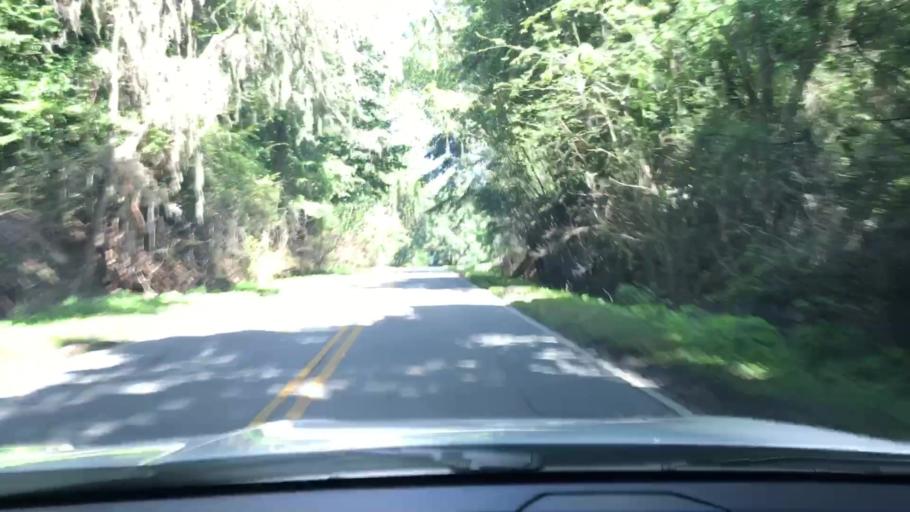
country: US
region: South Carolina
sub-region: Berkeley County
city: Ladson
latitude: 32.8978
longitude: -80.1385
